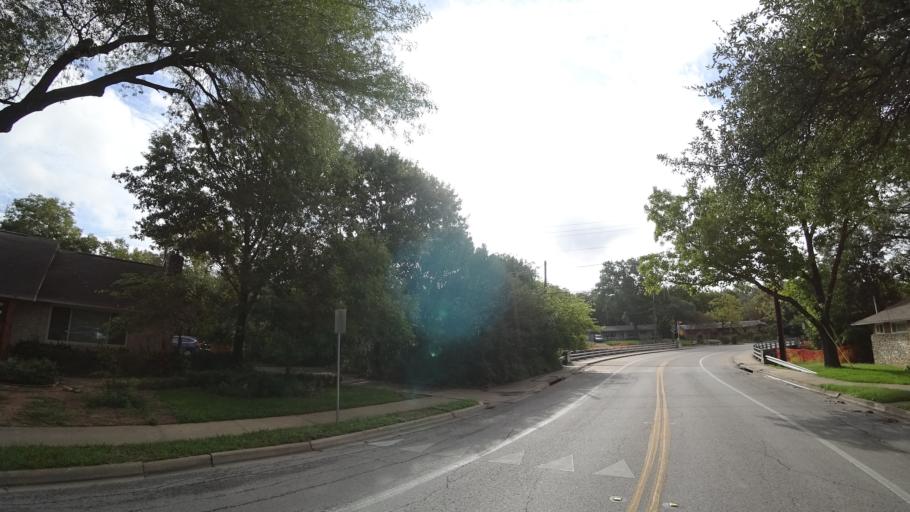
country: US
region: Texas
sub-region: Travis County
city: West Lake Hills
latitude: 30.3465
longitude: -97.7455
